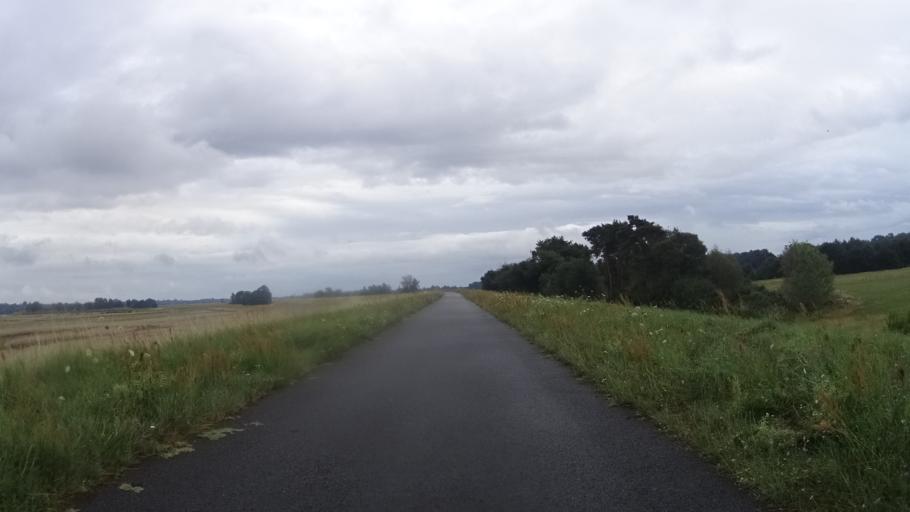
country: FR
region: Centre
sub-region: Departement du Loiret
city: Sandillon
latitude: 47.8546
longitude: 2.0575
